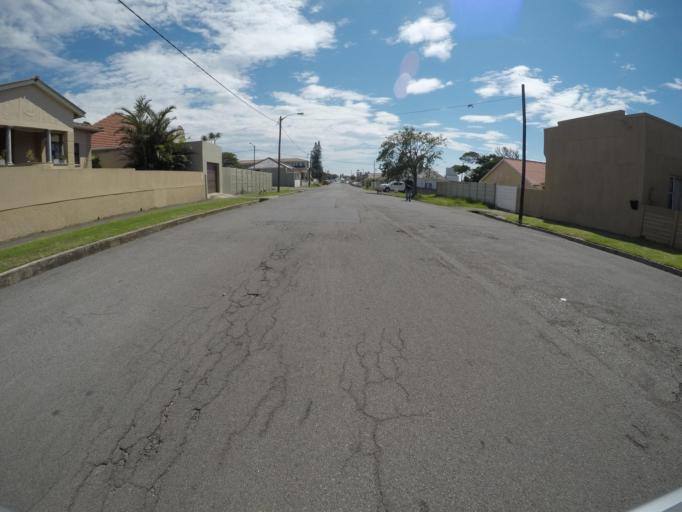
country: ZA
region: Eastern Cape
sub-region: Buffalo City Metropolitan Municipality
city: East London
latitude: -33.0362
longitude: 27.9046
